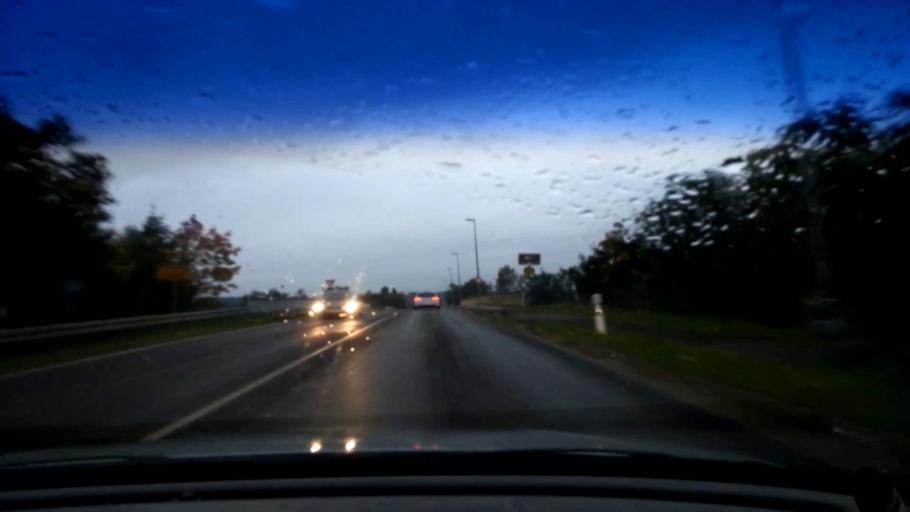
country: DE
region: Bavaria
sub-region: Upper Franconia
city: Viereth-Trunstadt
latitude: 49.9248
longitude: 10.7728
